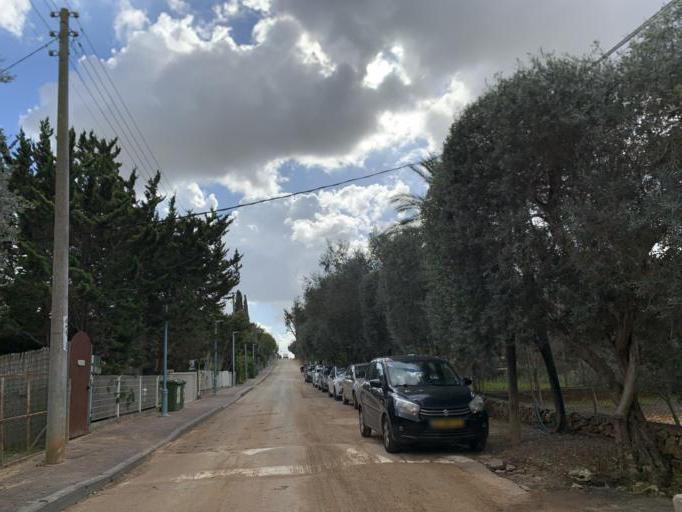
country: IL
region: Central District
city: Hod HaSharon
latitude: 32.1705
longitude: 34.8961
